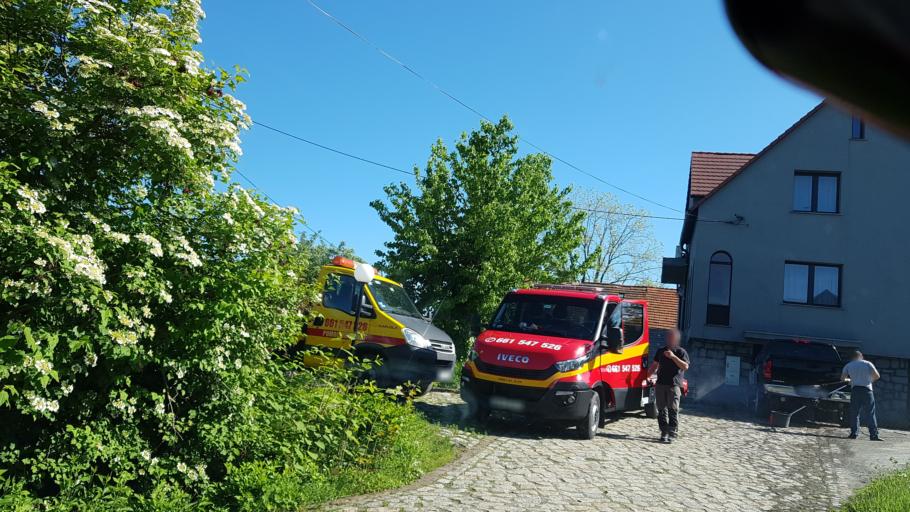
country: PL
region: Lower Silesian Voivodeship
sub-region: Powiat zabkowicki
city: Budzow
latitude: 50.5748
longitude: 16.6692
